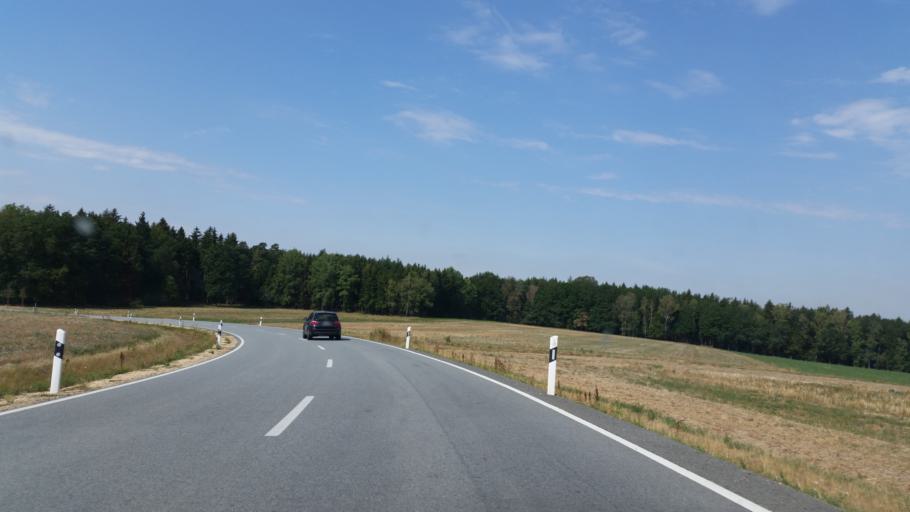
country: DE
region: Saxony
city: Grosshennersdorf
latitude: 50.9815
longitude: 14.7615
